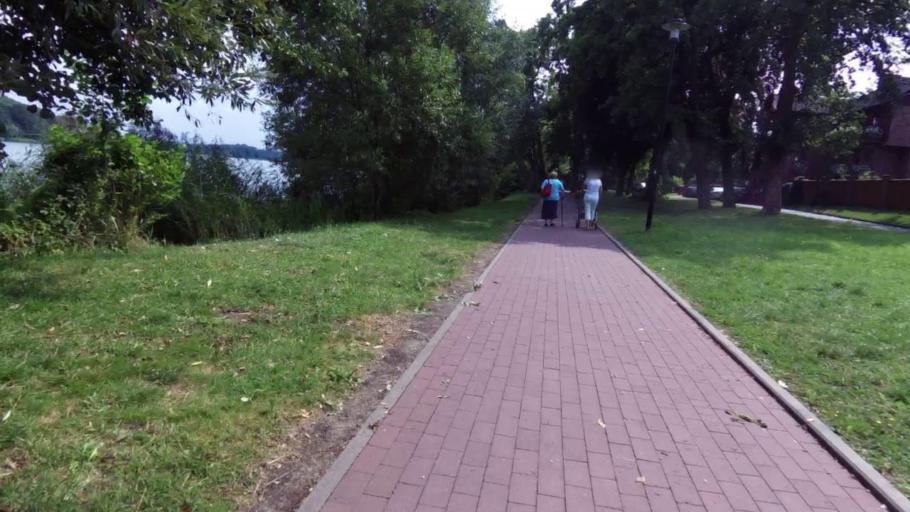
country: PL
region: West Pomeranian Voivodeship
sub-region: Powiat choszczenski
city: Choszczno
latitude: 53.1648
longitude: 15.4083
